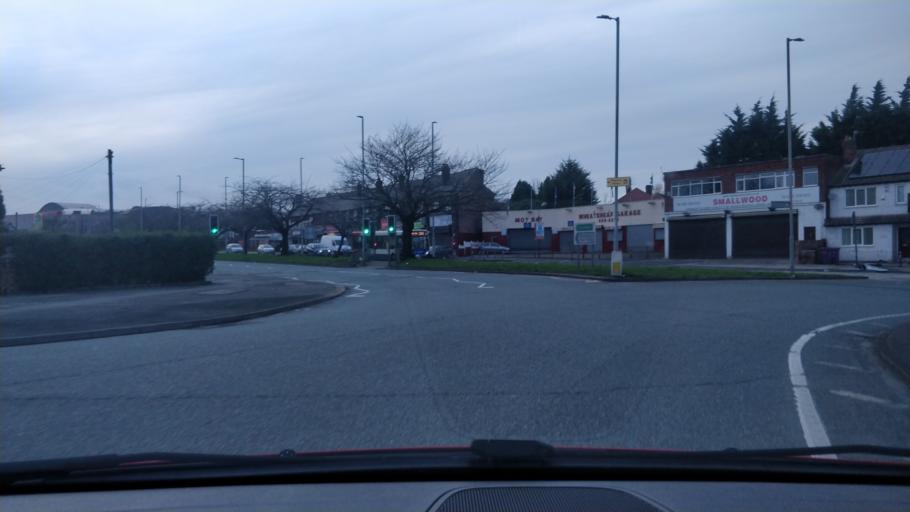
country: GB
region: England
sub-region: Knowsley
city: Knowsley
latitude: 53.4186
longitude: -2.8889
